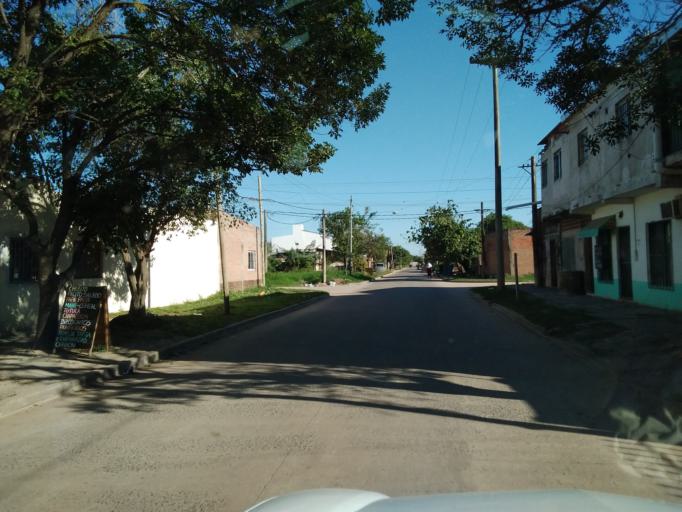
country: AR
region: Corrientes
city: Corrientes
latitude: -27.4700
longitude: -58.7911
